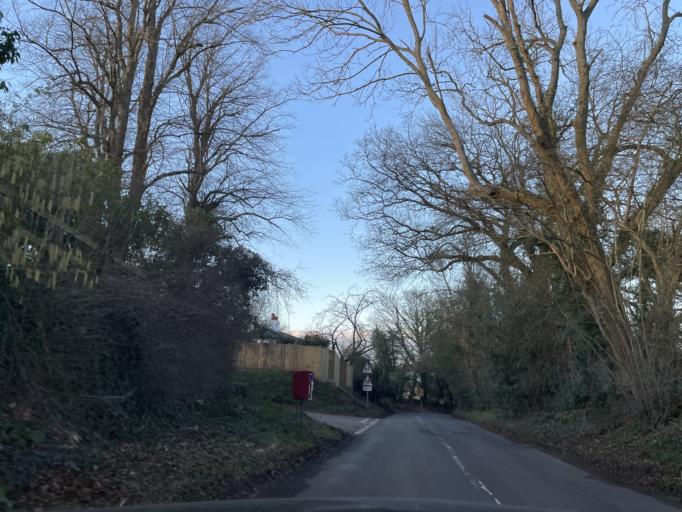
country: GB
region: England
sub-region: Kent
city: Halstead
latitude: 51.2723
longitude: 0.1267
